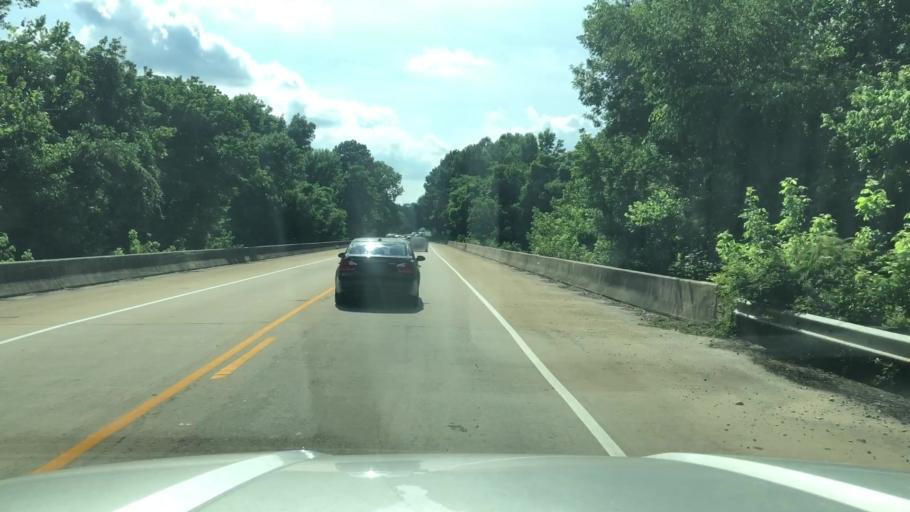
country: US
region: Georgia
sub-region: Douglas County
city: Lithia Springs
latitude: 33.6932
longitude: -84.6293
